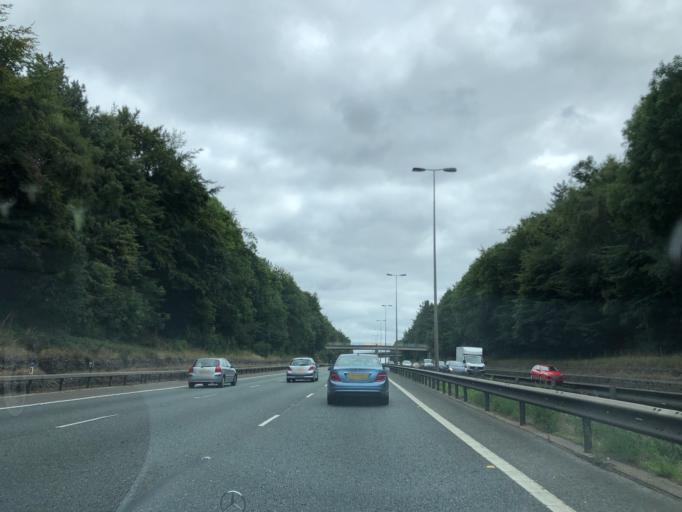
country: GB
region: England
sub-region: Buckinghamshire
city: Marlow
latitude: 51.6240
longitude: -0.8236
